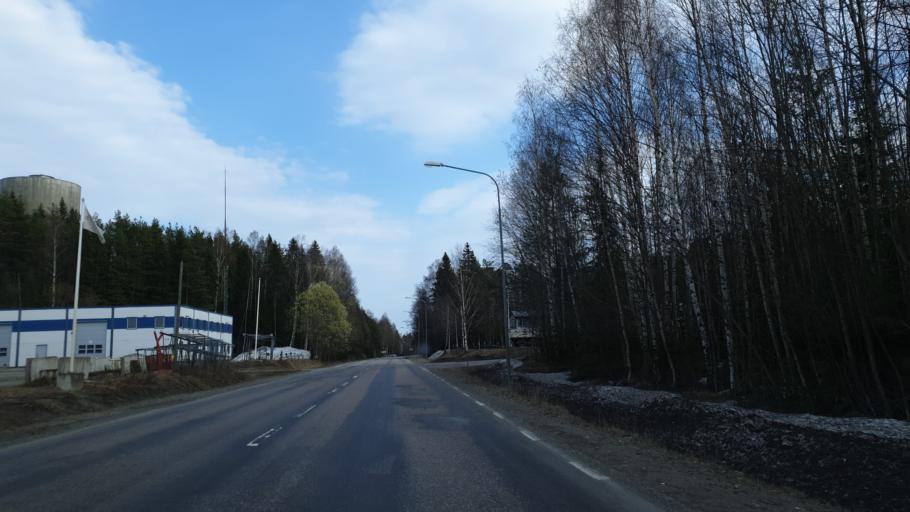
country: SE
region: Gaevleborg
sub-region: Hudiksvalls Kommun
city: Iggesund
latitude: 61.6439
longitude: 17.0587
